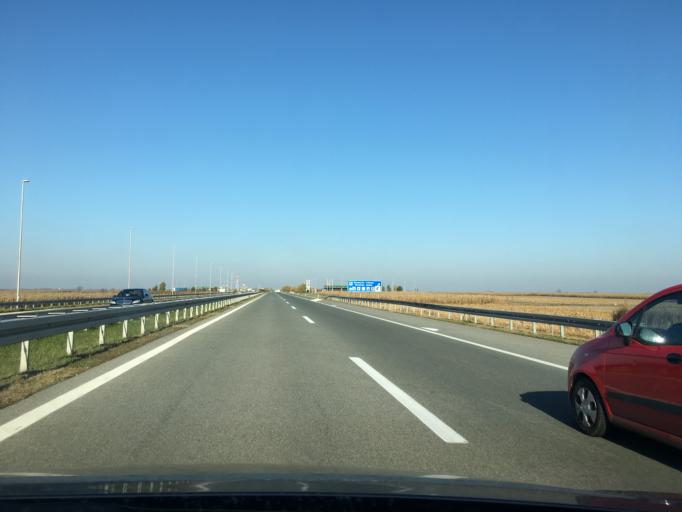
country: RS
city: Rumenka
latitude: 45.3249
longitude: 19.7850
